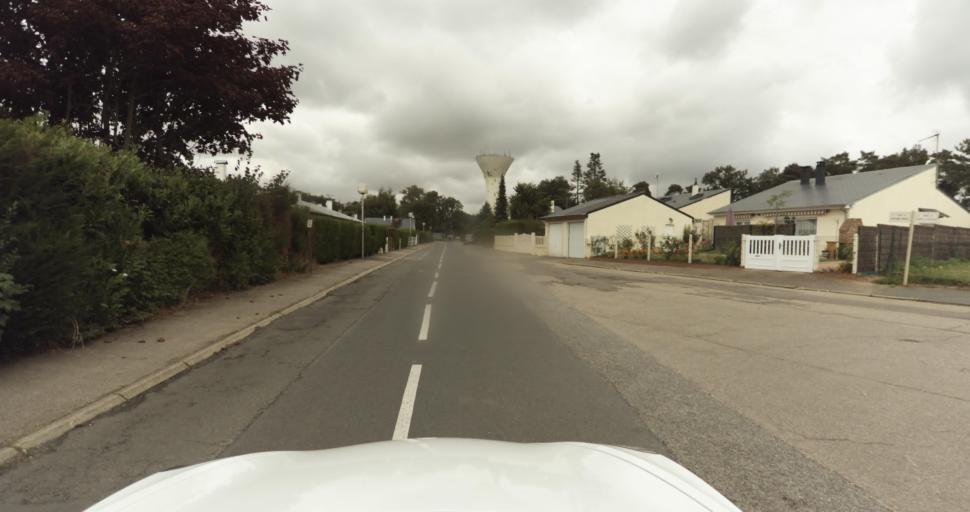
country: FR
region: Haute-Normandie
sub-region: Departement de l'Eure
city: Saint-Sebastien-de-Morsent
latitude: 49.0066
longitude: 1.0937
